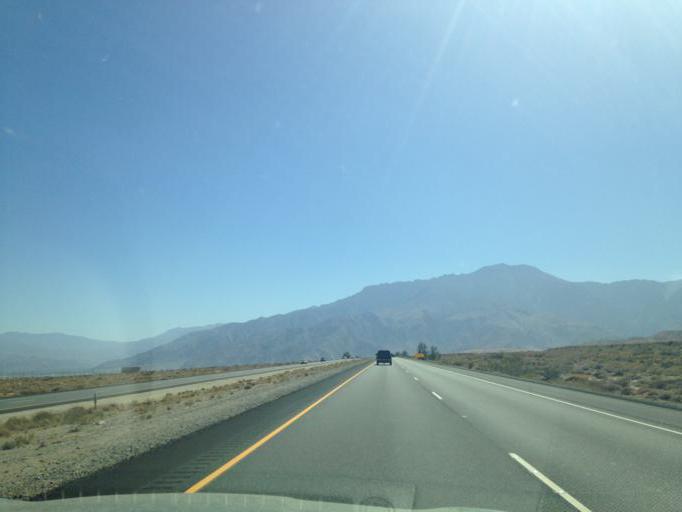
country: US
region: California
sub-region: San Bernardino County
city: Morongo Valley
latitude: 33.9797
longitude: -116.5848
